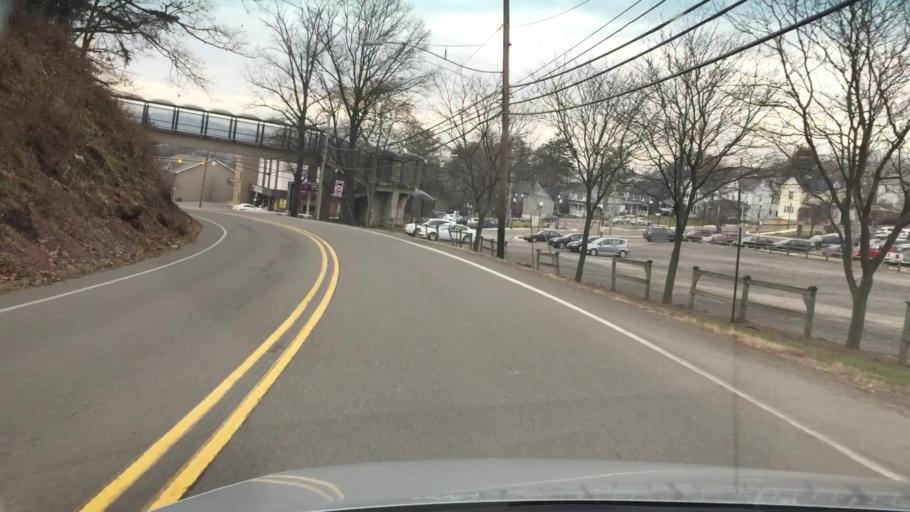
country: US
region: Pennsylvania
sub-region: Columbia County
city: Bloomsburg
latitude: 41.0084
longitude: -76.4510
